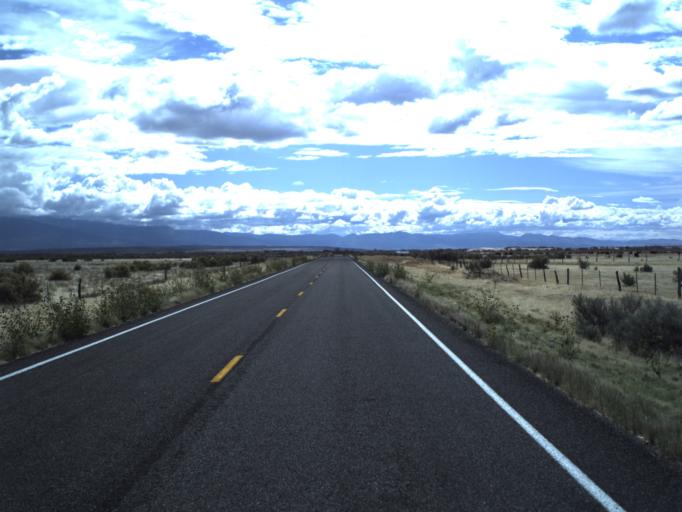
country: US
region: Utah
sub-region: Millard County
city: Fillmore
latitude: 39.1463
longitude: -112.4098
